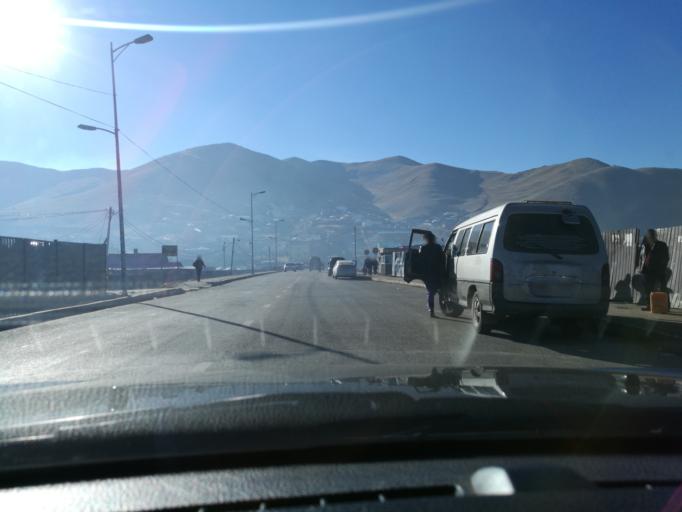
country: MN
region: Ulaanbaatar
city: Ulaanbaatar
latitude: 47.9799
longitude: 106.9384
